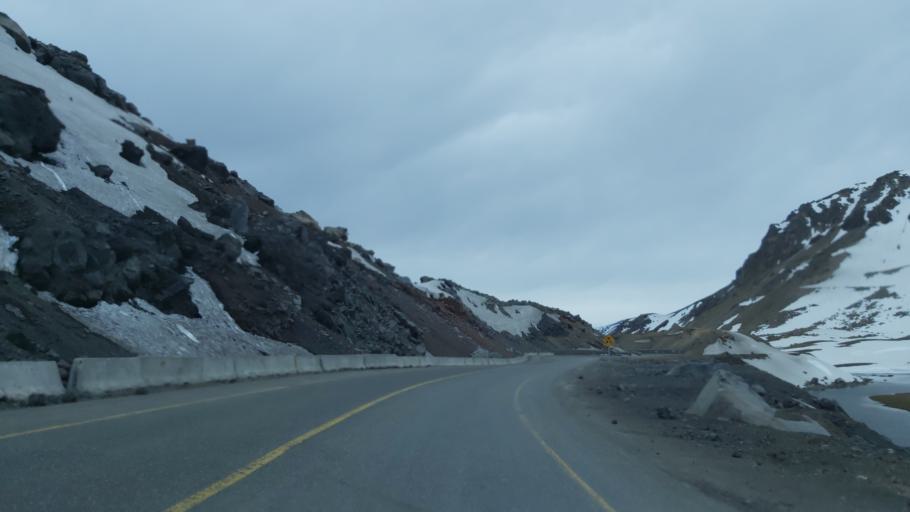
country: CL
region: Maule
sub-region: Provincia de Linares
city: Colbun
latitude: -36.0061
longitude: -70.5588
